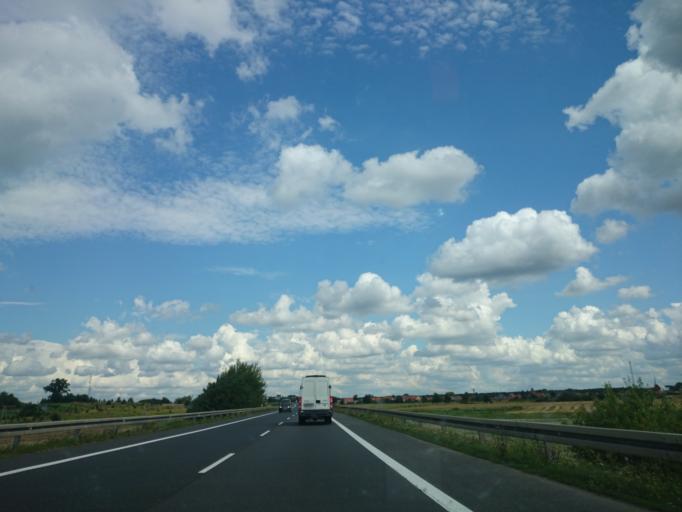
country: PL
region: Lower Silesian Voivodeship
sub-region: Legnica
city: Legnica
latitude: 51.2438
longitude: 16.1468
